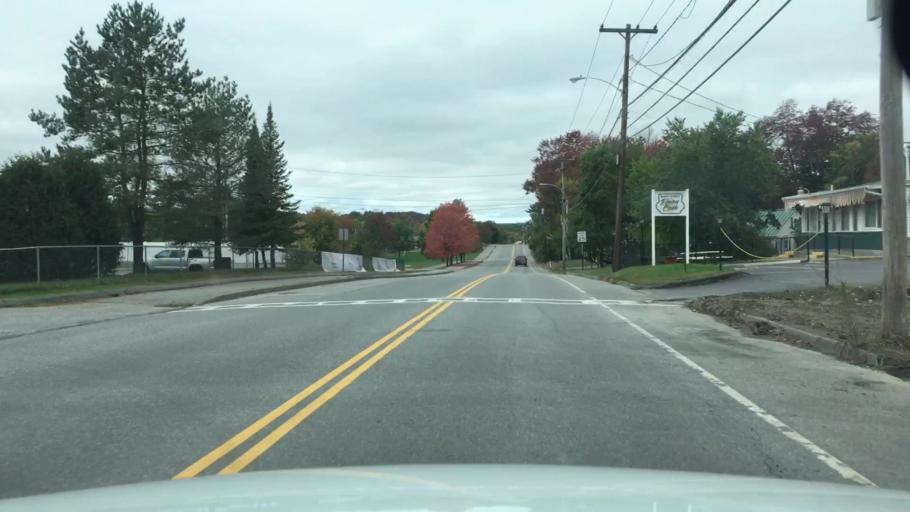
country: US
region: Maine
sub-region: Kennebec County
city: Waterville
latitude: 44.5607
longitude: -69.6429
